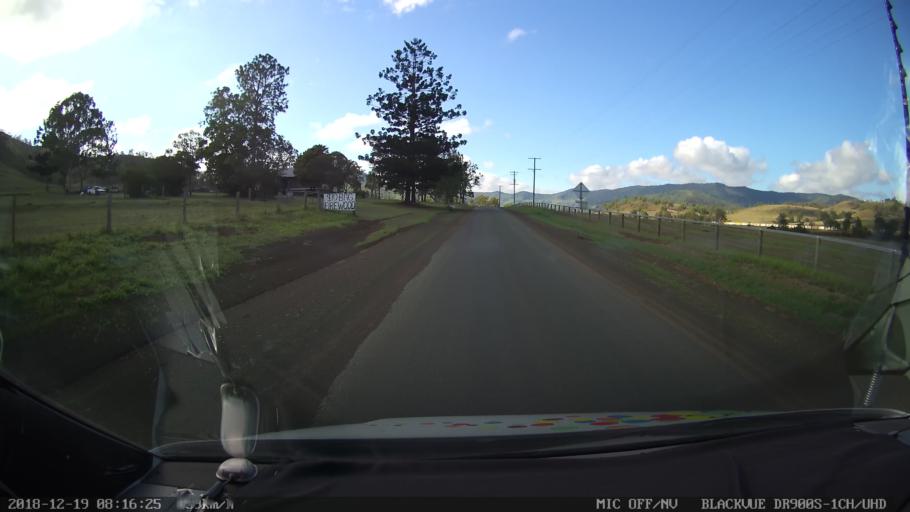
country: AU
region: New South Wales
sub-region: Kyogle
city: Kyogle
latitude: -28.2575
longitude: 152.9064
